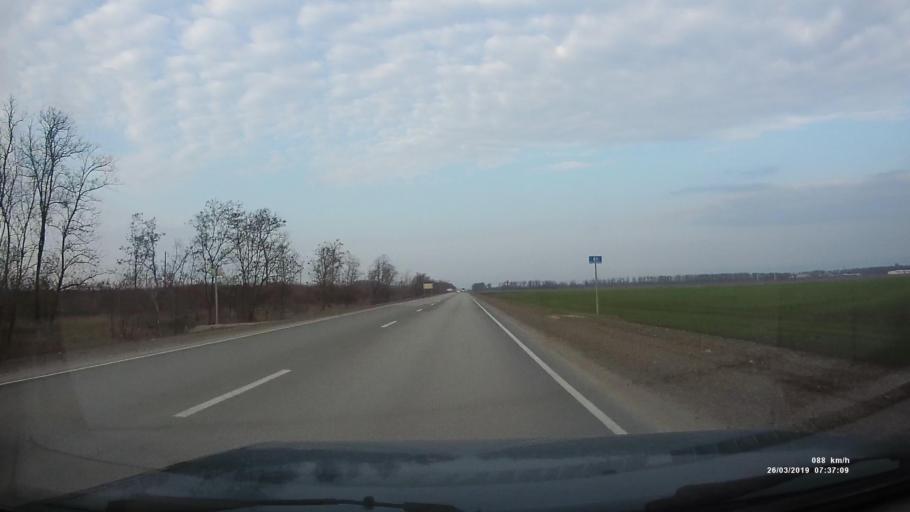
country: RU
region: Rostov
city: Novobessergenovka
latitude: 47.2034
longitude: 38.7066
